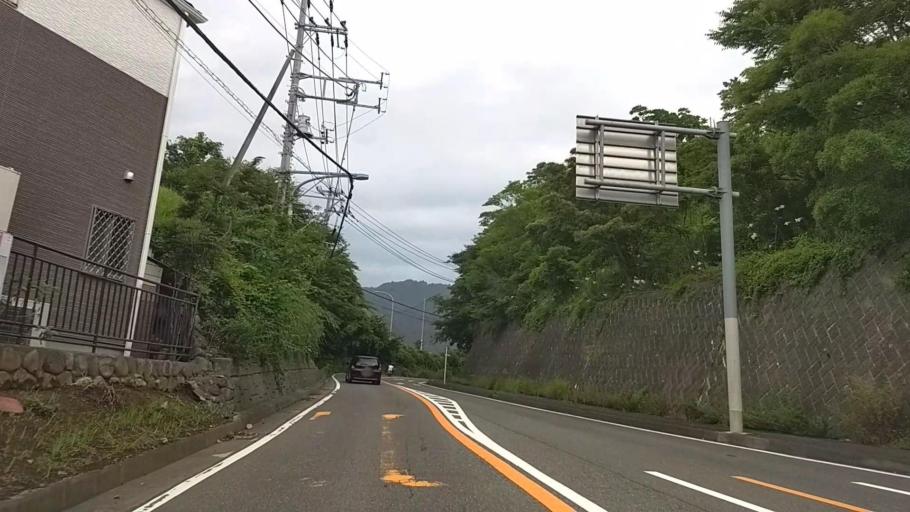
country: JP
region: Kanagawa
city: Hadano
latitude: 35.3431
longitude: 139.1581
